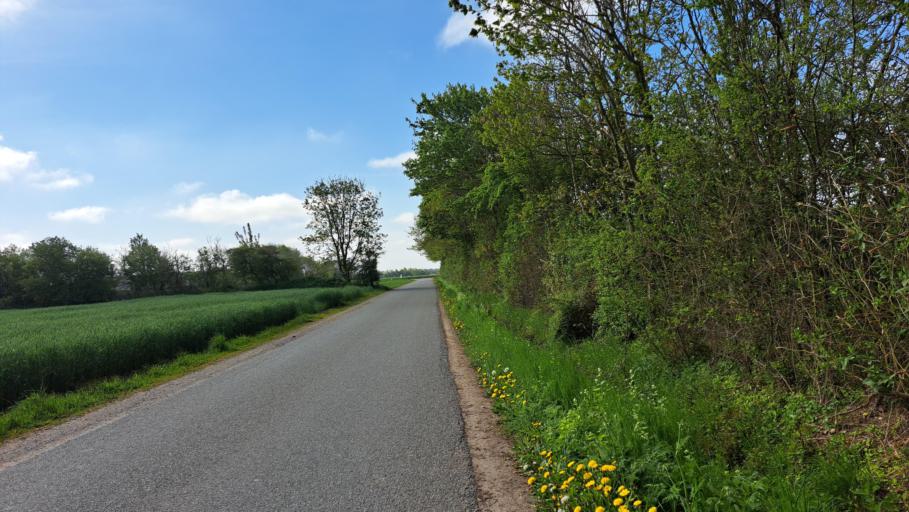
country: DK
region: Central Jutland
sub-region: Hedensted Kommune
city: Hedensted
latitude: 55.8022
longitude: 9.6558
